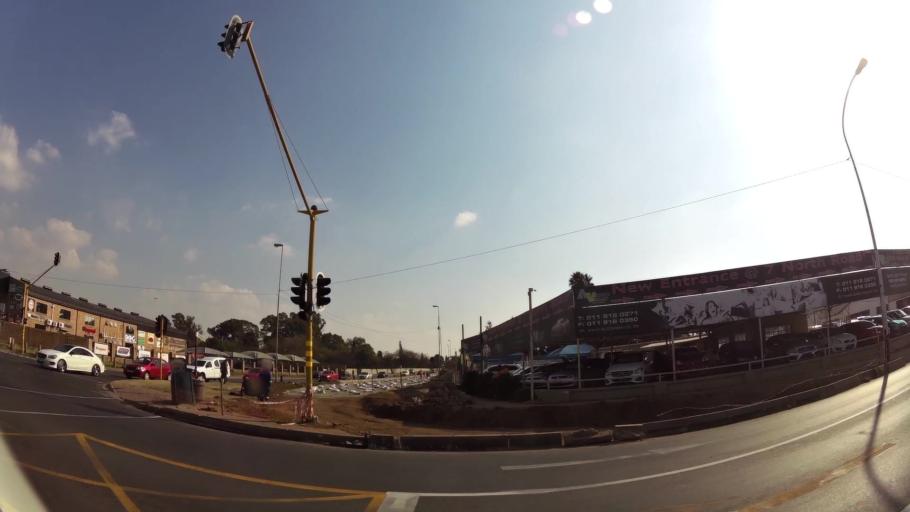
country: ZA
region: Gauteng
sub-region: Ekurhuleni Metropolitan Municipality
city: Boksburg
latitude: -26.1915
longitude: 28.2538
